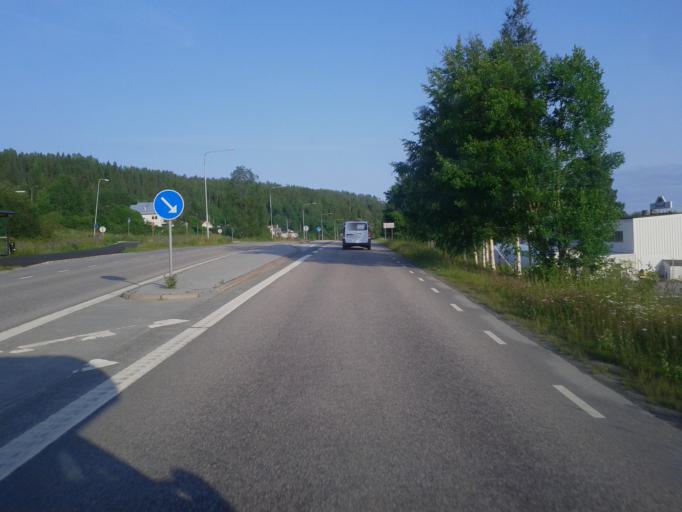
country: SE
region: Vaesternorrland
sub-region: OErnskoeldsviks Kommun
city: Ornskoldsvik
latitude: 63.2820
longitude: 18.7413
